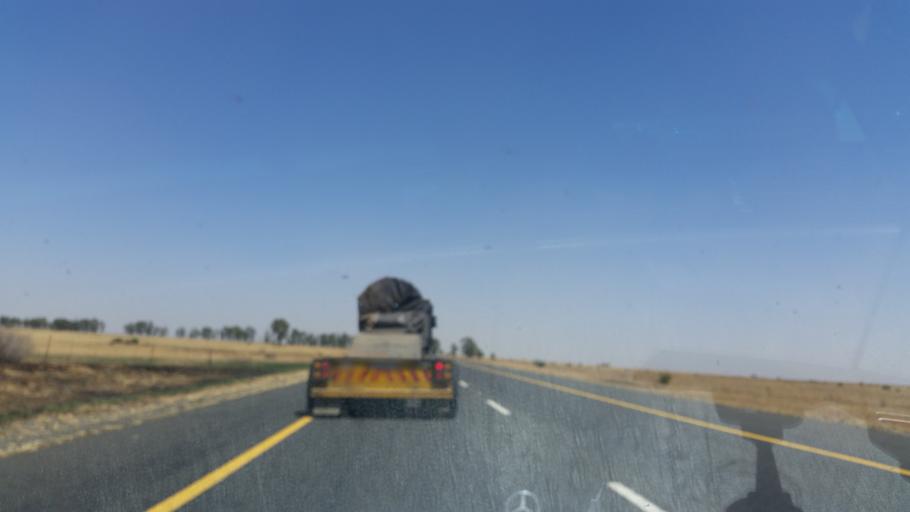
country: ZA
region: Orange Free State
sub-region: Lejweleputswa District Municipality
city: Winburg
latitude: -28.6372
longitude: 26.8954
